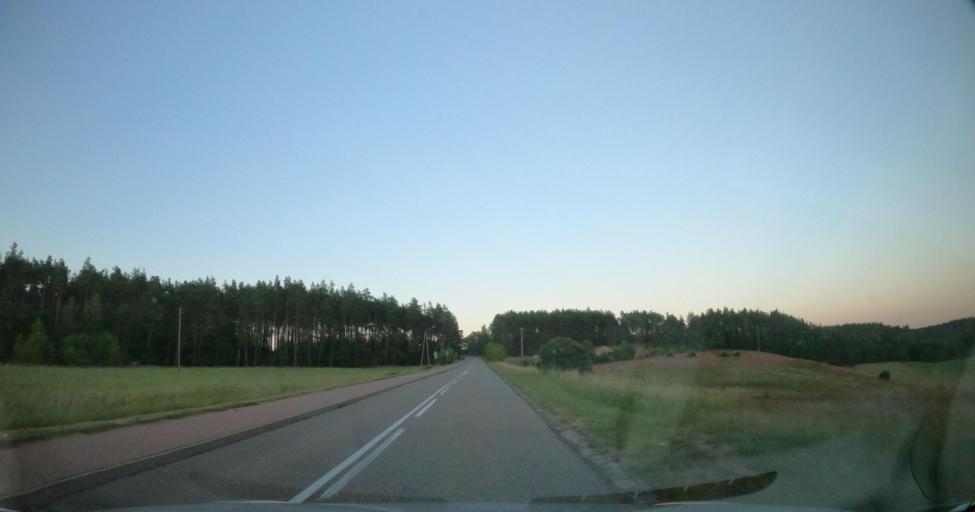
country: PL
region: Pomeranian Voivodeship
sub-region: Powiat wejherowski
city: Linia
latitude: 54.4573
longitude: 18.0080
